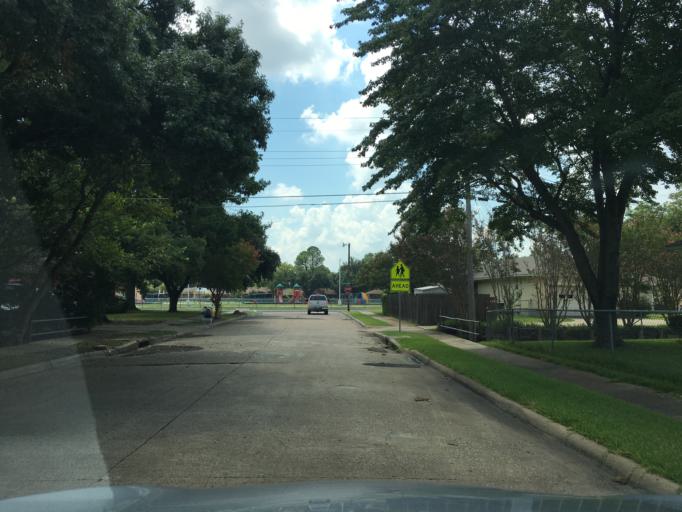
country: US
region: Texas
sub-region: Dallas County
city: Garland
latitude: 32.9356
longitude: -96.6466
